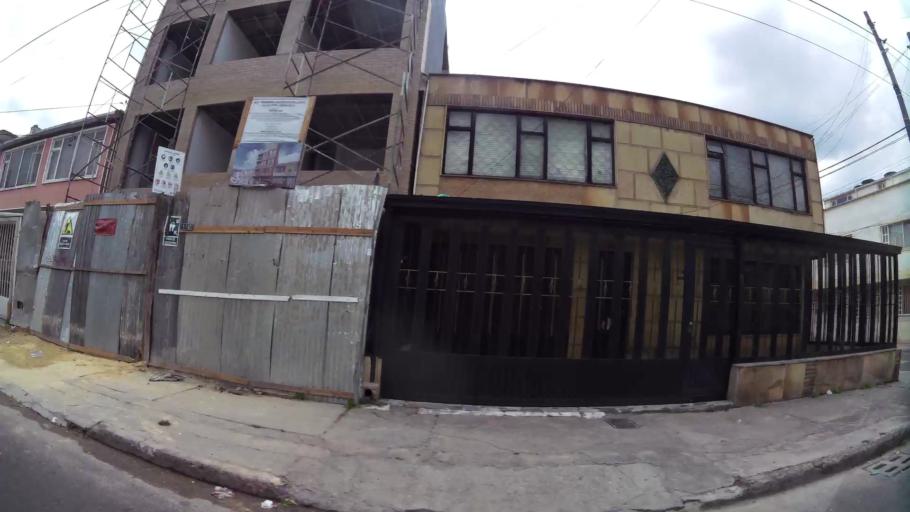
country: CO
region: Bogota D.C.
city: Bogota
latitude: 4.5965
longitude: -74.0988
